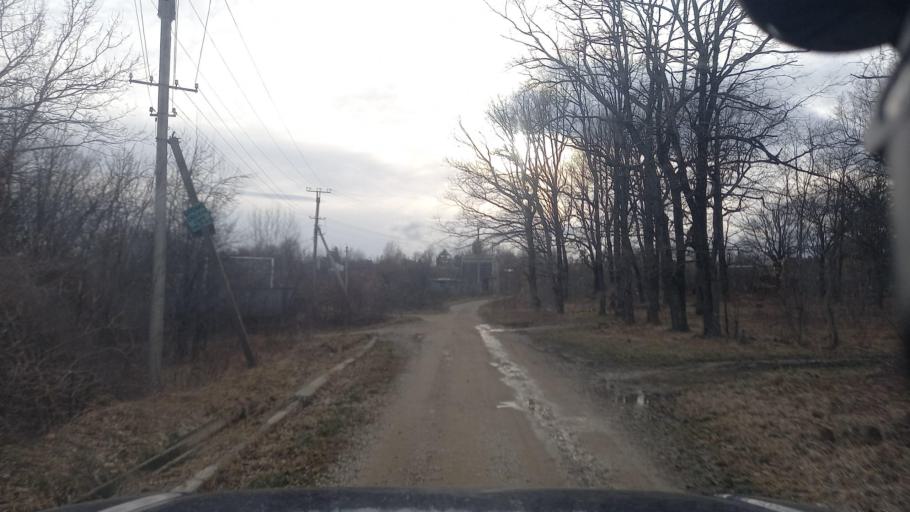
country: RU
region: Krasnodarskiy
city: Goryachiy Klyuch
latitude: 44.6951
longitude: 39.0195
